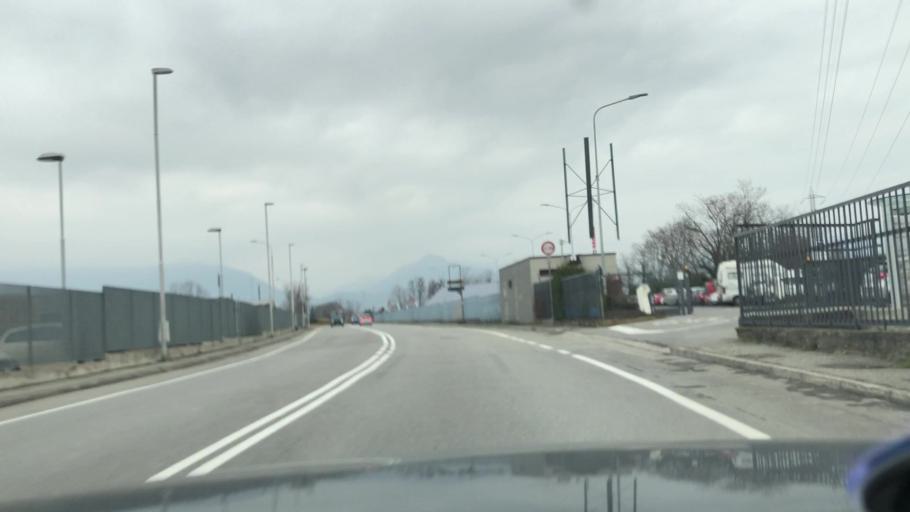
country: IT
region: Lombardy
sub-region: Provincia di Bergamo
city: Ponte San Pietro
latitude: 45.7063
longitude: 9.5838
